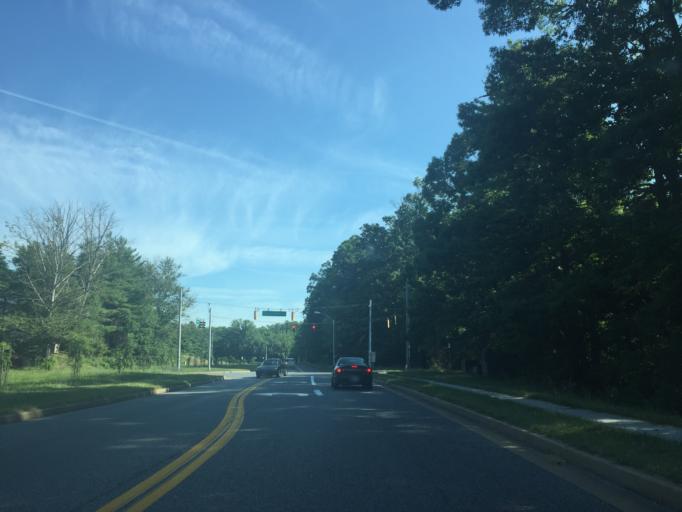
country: US
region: Maryland
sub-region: Baltimore County
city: Perry Hall
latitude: 39.3847
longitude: -76.4696
